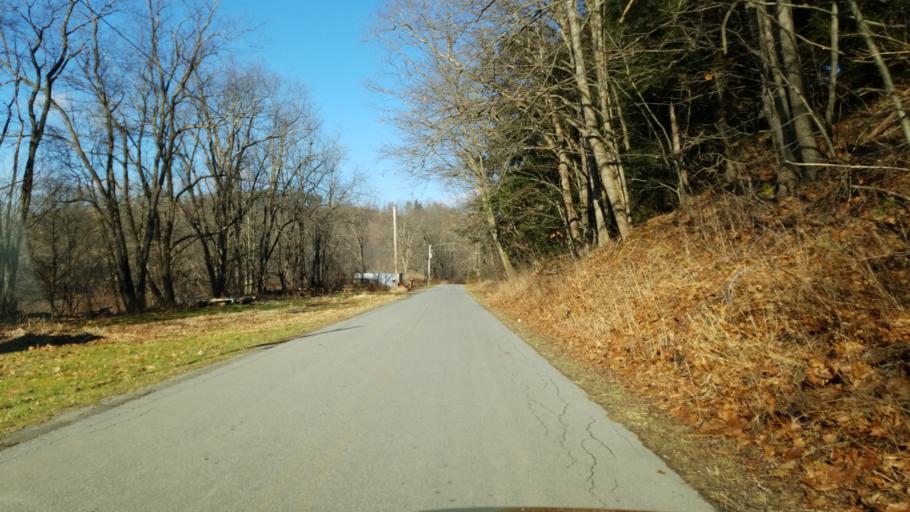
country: US
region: Pennsylvania
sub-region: Clearfield County
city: Curwensville
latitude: 40.9770
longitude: -78.4922
